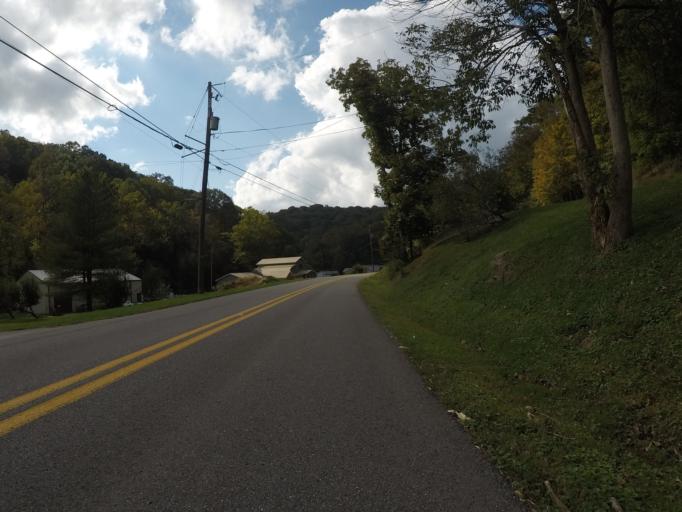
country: US
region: West Virginia
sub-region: Wayne County
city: Lavalette
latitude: 38.3514
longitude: -82.4411
